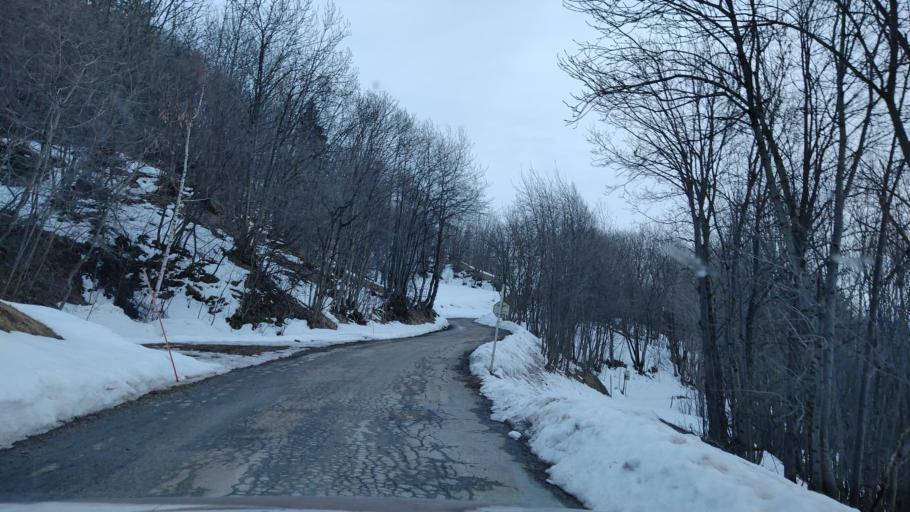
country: FR
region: Rhone-Alpes
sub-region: Departement de la Savoie
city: Saint-Michel-de-Maurienne
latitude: 45.2485
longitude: 6.4734
